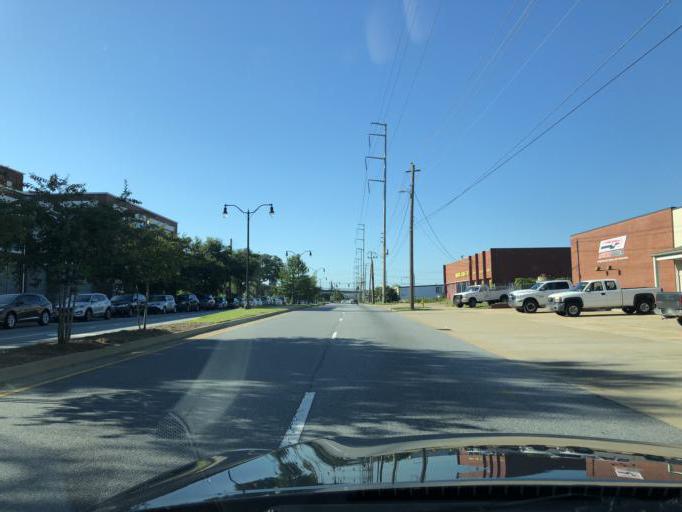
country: US
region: Georgia
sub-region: Muscogee County
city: Columbus
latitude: 32.4741
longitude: -84.9849
